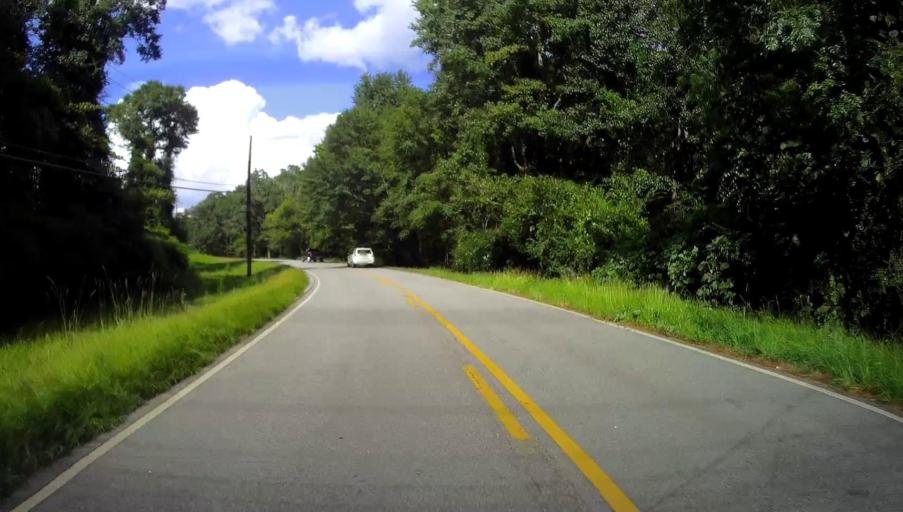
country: US
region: Georgia
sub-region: Harris County
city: Hamilton
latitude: 32.5718
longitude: -84.8318
